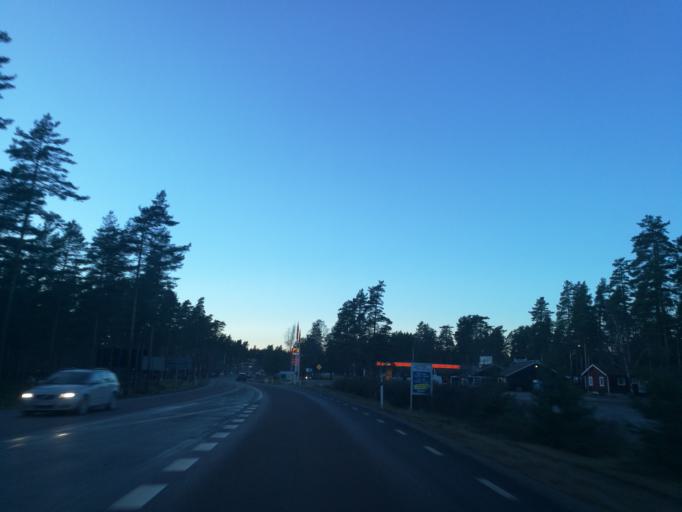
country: SE
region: Vaermland
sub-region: Eda Kommun
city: Charlottenberg
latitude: 59.9301
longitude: 12.2446
